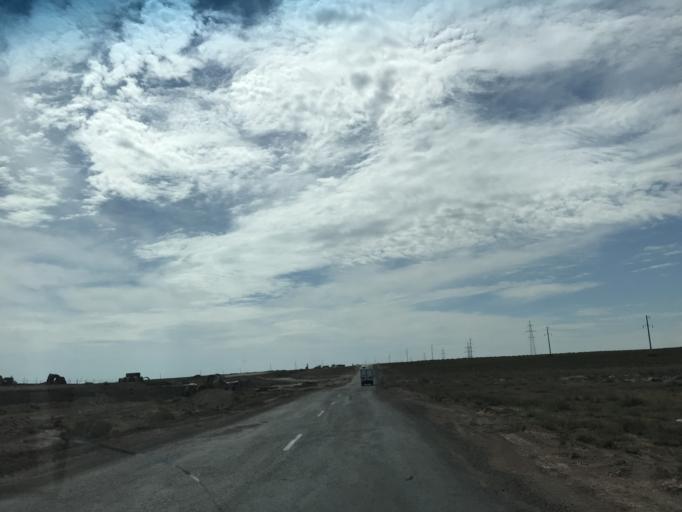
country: KZ
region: Almaty Oblysy
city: Ulken
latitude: 45.2551
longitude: 73.8063
